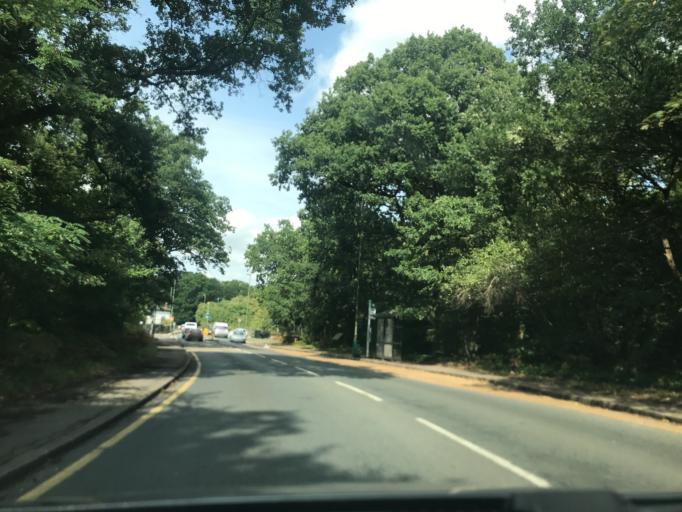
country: GB
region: England
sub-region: Surrey
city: Weybridge
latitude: 51.3607
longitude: -0.4567
